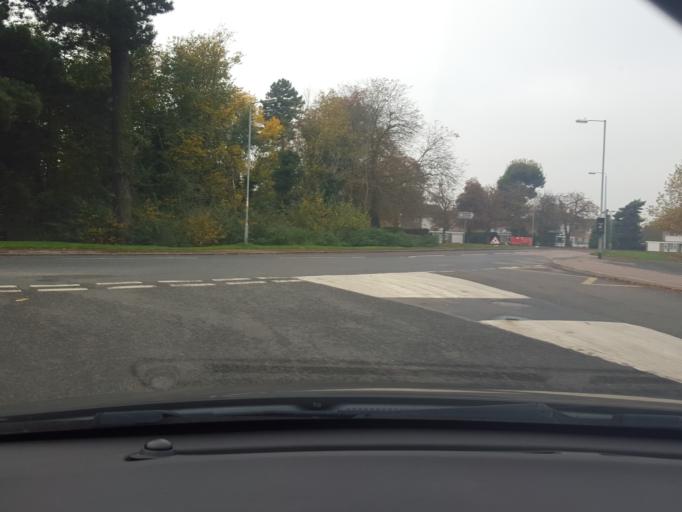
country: GB
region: England
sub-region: Essex
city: Brightlingsea
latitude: 51.8193
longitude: 1.0224
